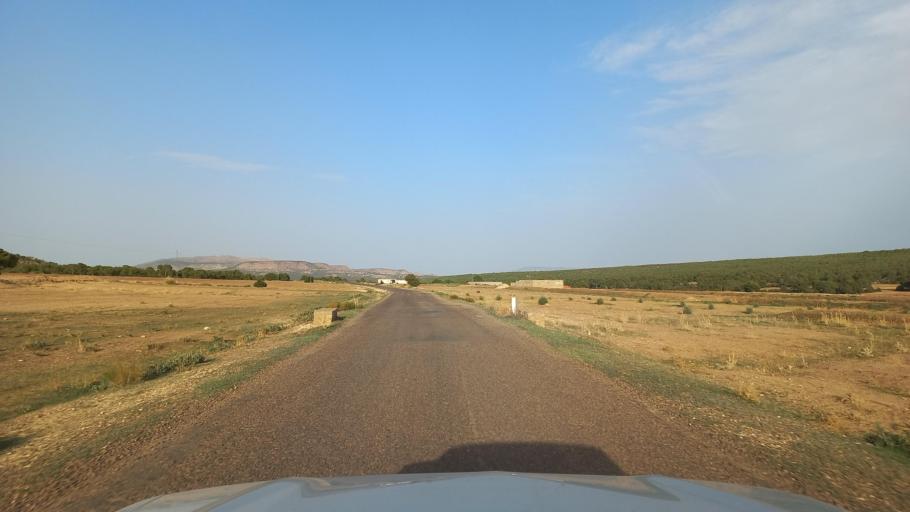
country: TN
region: Al Qasrayn
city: Kasserine
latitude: 35.3959
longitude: 8.8803
